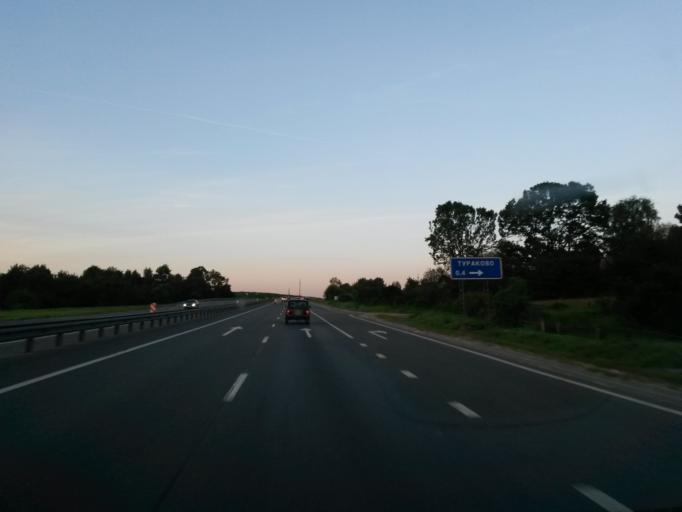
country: RU
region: Moskovskaya
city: Sergiyev Posad
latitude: 56.2775
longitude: 38.2021
